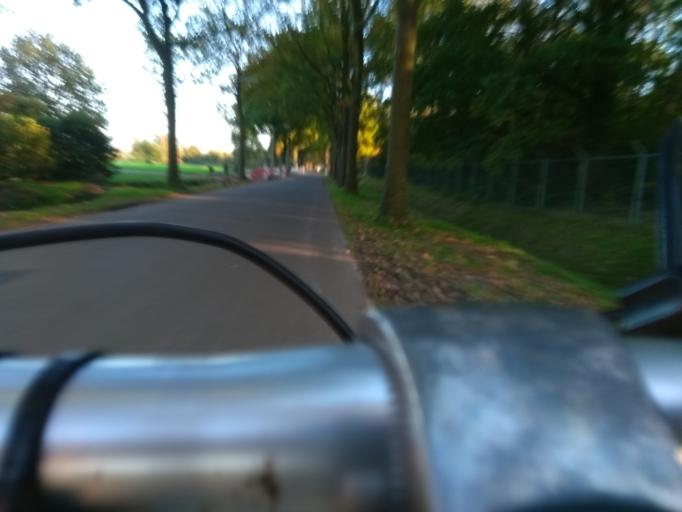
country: NL
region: Drenthe
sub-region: Gemeente Assen
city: Assen
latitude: 52.9780
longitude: 6.5222
